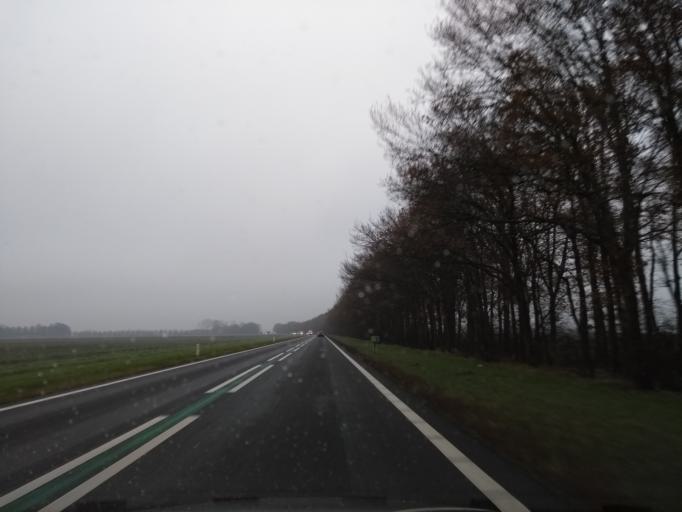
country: NL
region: Overijssel
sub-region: Gemeente Twenterand
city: Westerhaar-Vriezenveensewijk
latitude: 52.4820
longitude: 6.6102
